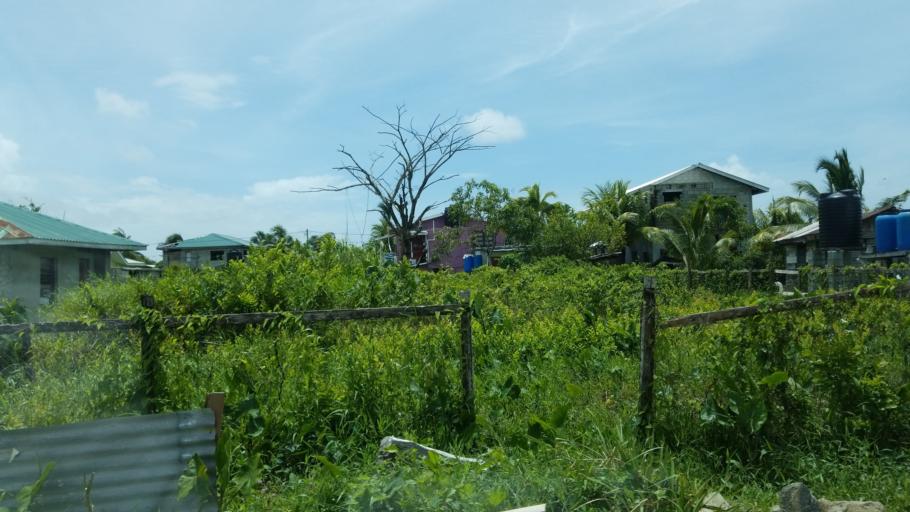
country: GY
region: Demerara-Mahaica
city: Georgetown
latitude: 6.7922
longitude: -58.1237
